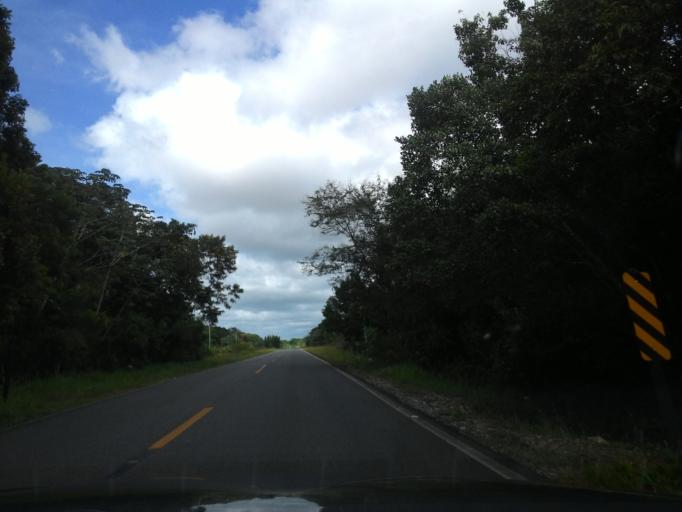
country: BR
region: Sao Paulo
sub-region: Iguape
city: Iguape
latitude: -24.7585
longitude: -47.6339
